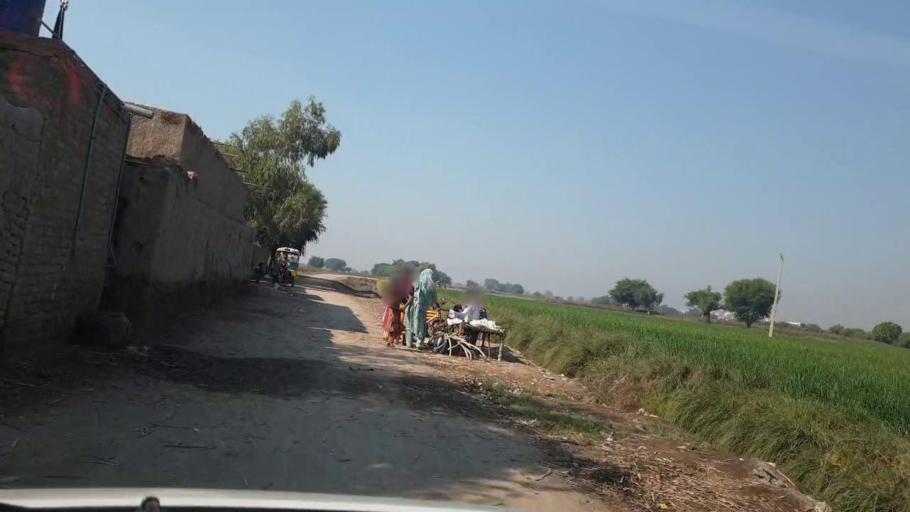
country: PK
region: Sindh
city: Bhan
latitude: 26.6418
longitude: 67.7144
